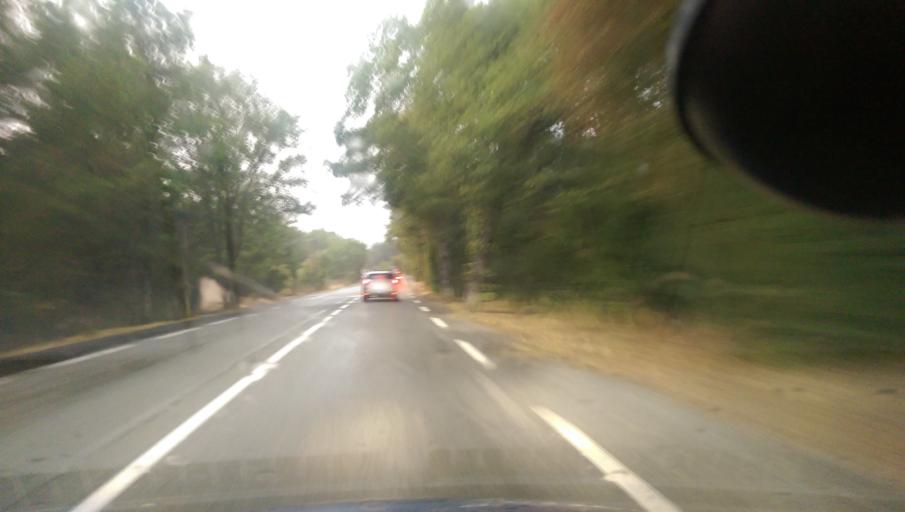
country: FR
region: Provence-Alpes-Cote d'Azur
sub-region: Departement des Alpes-Maritimes
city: Saint-Vallier-de-Thiey
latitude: 43.6884
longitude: 6.8719
